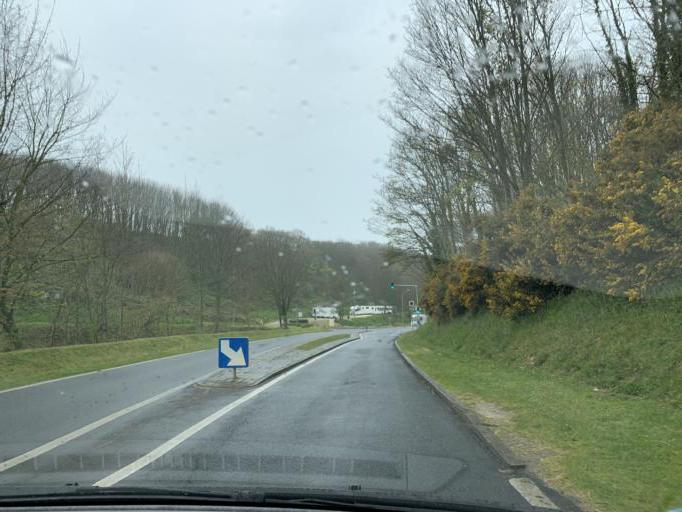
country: FR
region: Haute-Normandie
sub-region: Departement de la Seine-Maritime
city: Etretat
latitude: 49.7002
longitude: 0.2005
